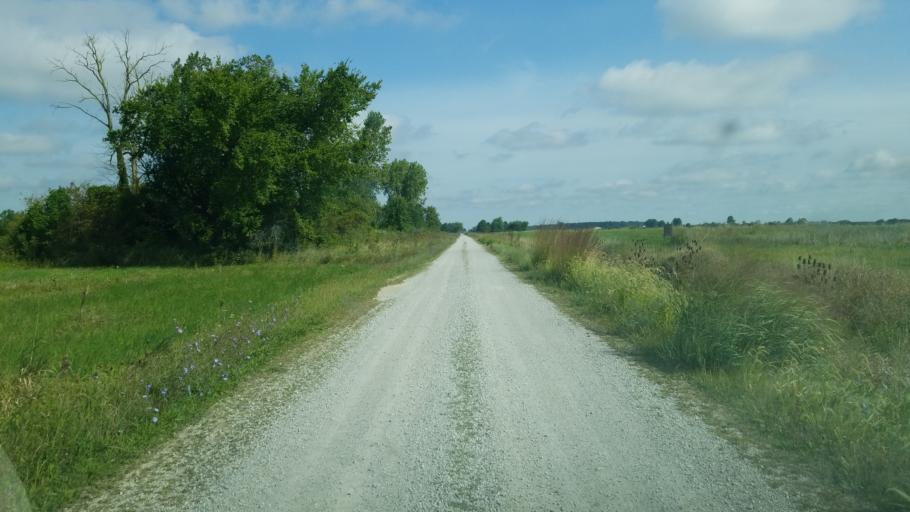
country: US
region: Ohio
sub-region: Wyandot County
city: Upper Sandusky
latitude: 40.7157
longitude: -83.3239
